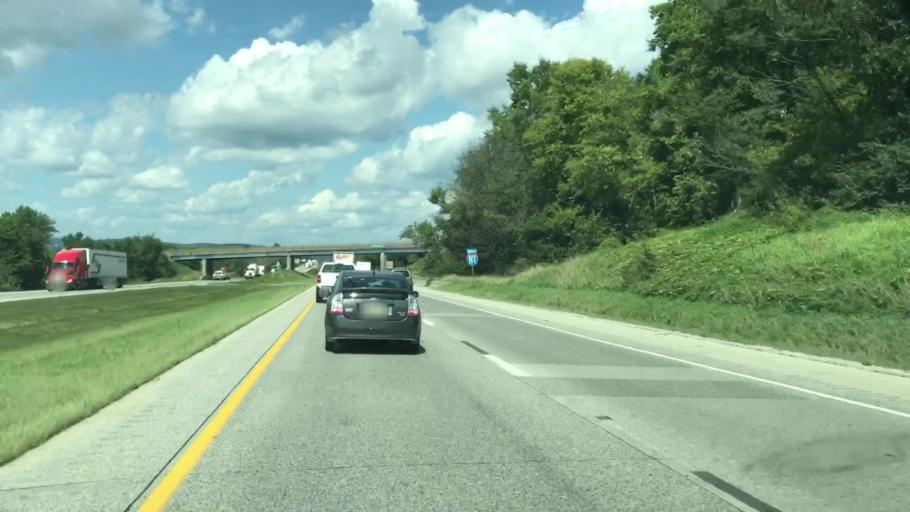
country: US
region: Pennsylvania
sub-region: Cumberland County
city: Carlisle
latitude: 40.2048
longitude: -77.1567
